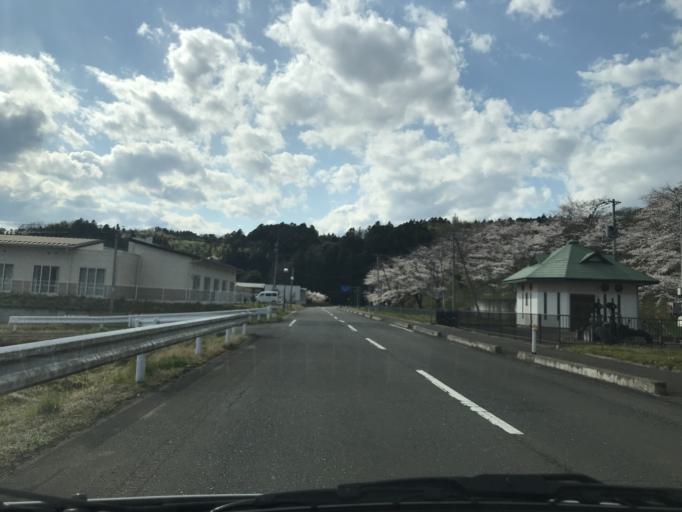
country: JP
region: Iwate
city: Ichinoseki
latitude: 38.7542
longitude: 141.1789
